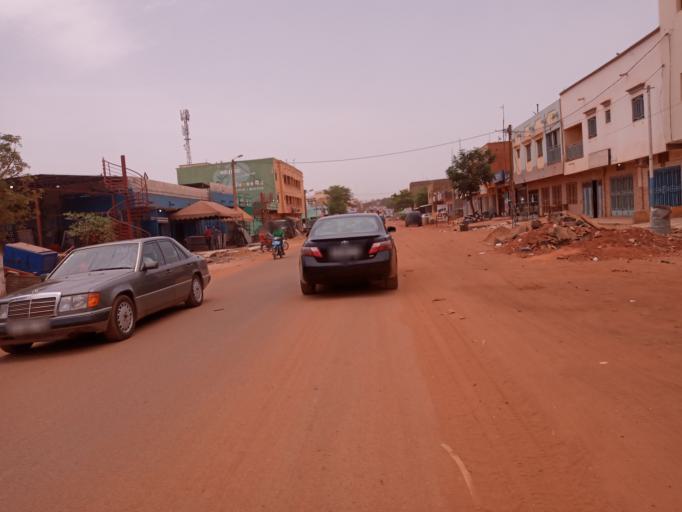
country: ML
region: Bamako
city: Bamako
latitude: 12.5774
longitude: -8.0131
